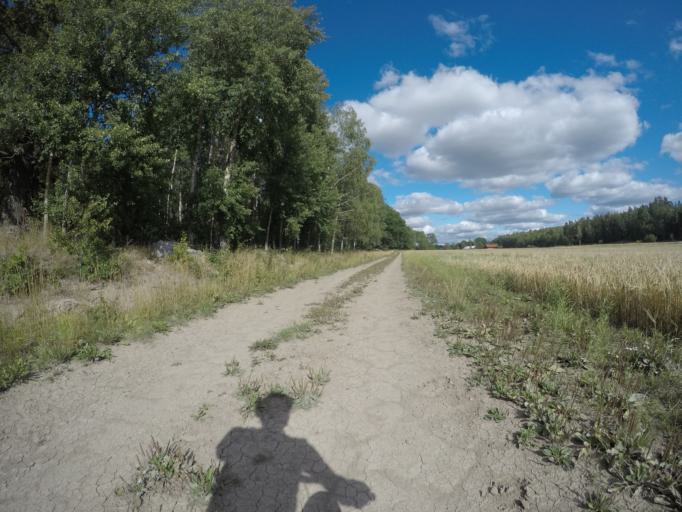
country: SE
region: Vaestmanland
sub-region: Hallstahammars Kommun
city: Kolback
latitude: 59.5163
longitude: 16.1972
